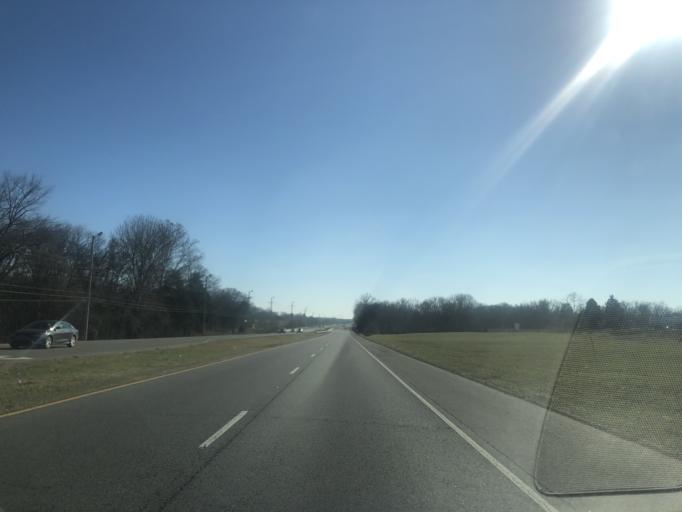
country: US
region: Tennessee
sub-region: Rutherford County
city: Smyrna
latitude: 35.9176
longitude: -86.4619
